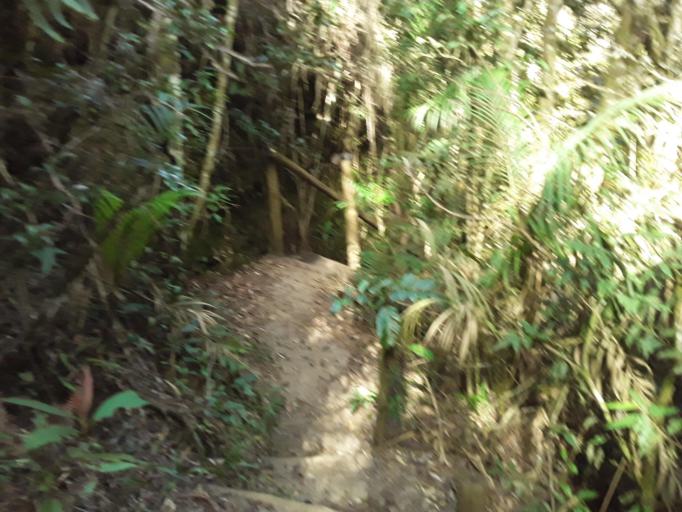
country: BR
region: Minas Gerais
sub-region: Lima Duarte
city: Lima Duarte
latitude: -21.7022
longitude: -43.8837
